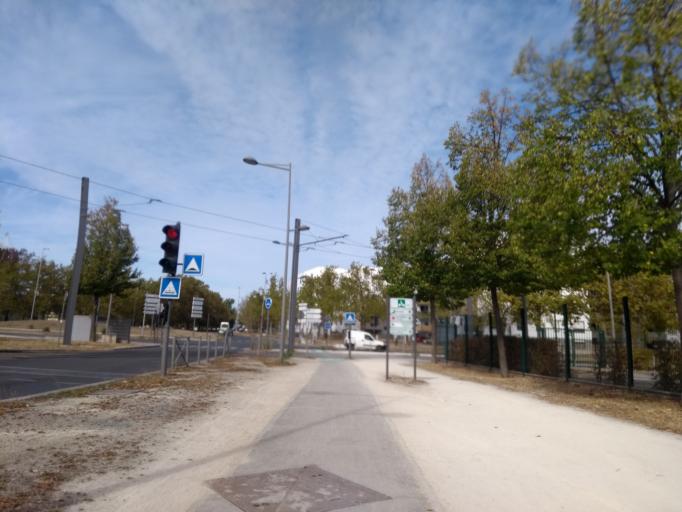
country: FR
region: Aquitaine
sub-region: Departement de la Gironde
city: Le Bouscat
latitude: 44.8736
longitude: -0.5762
